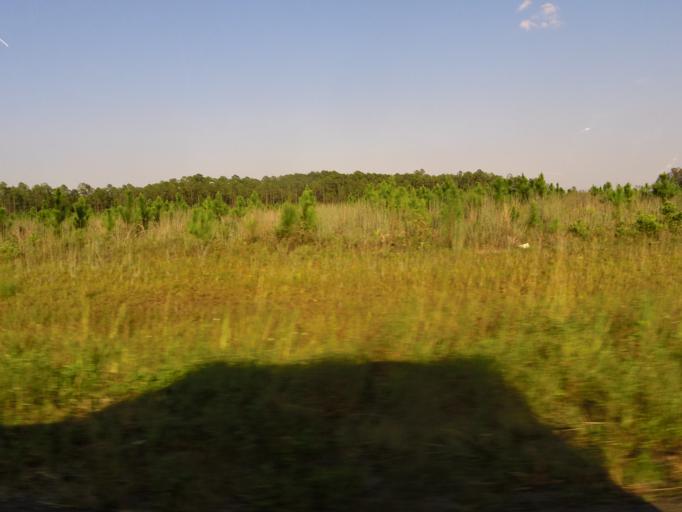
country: US
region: Florida
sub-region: Duval County
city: Baldwin
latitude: 30.3416
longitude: -82.0091
